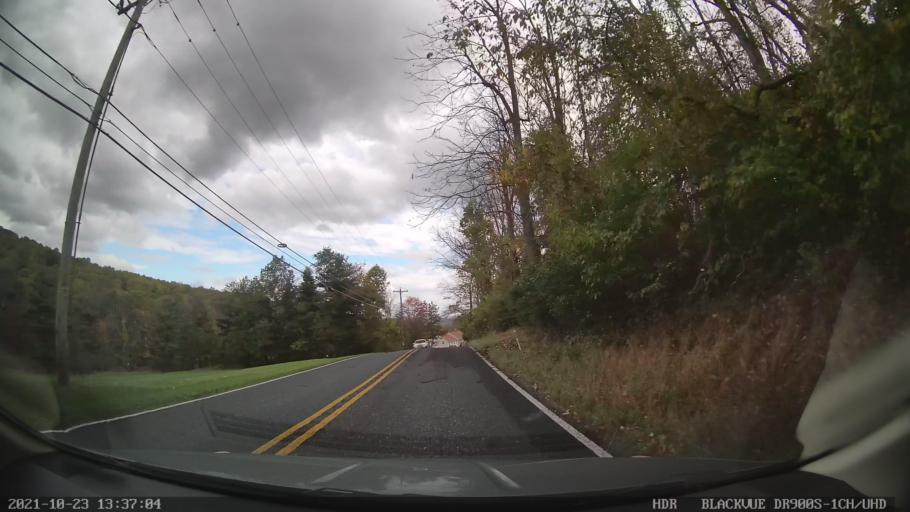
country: US
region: Pennsylvania
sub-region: Berks County
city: Bally
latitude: 40.4368
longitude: -75.5996
